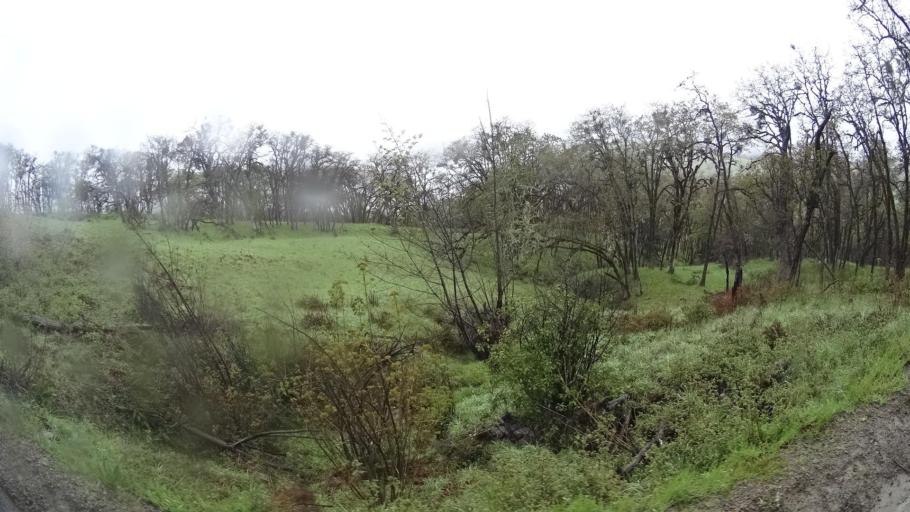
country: US
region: California
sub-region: Humboldt County
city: Westhaven-Moonstone
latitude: 41.1518
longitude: -123.8913
